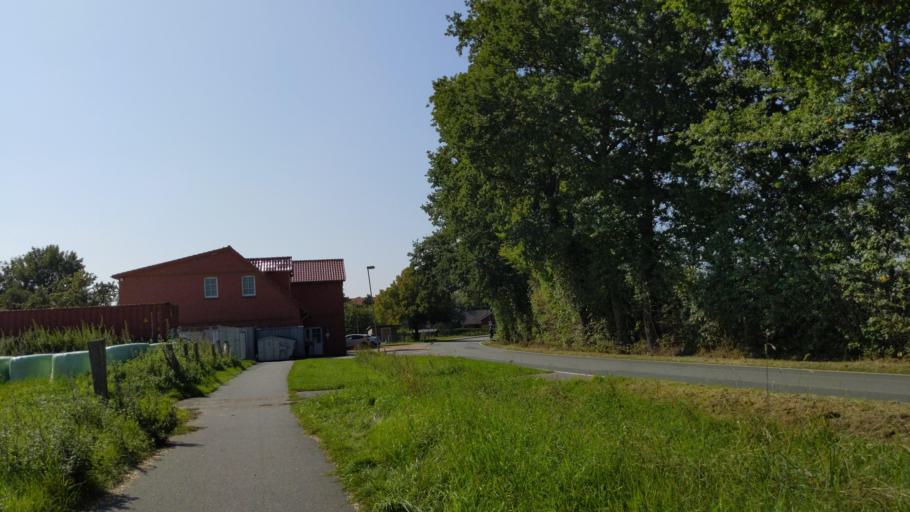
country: DE
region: Schleswig-Holstein
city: Gross Schenkenberg
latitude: 53.7945
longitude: 10.5743
